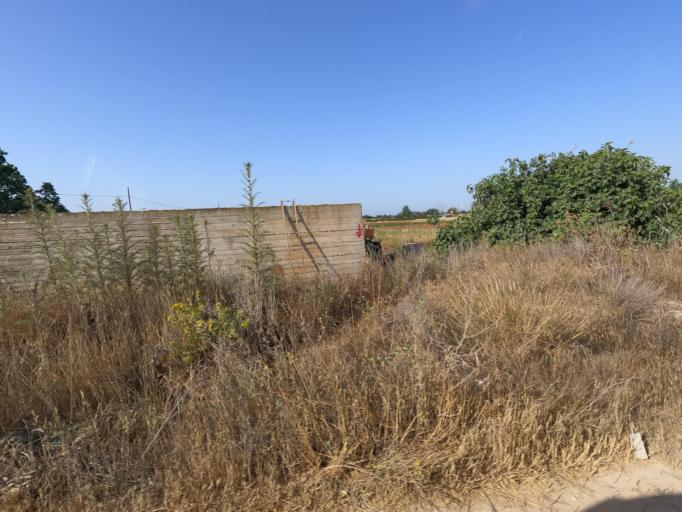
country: CY
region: Ammochostos
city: Frenaros
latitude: 35.0007
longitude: 33.9345
